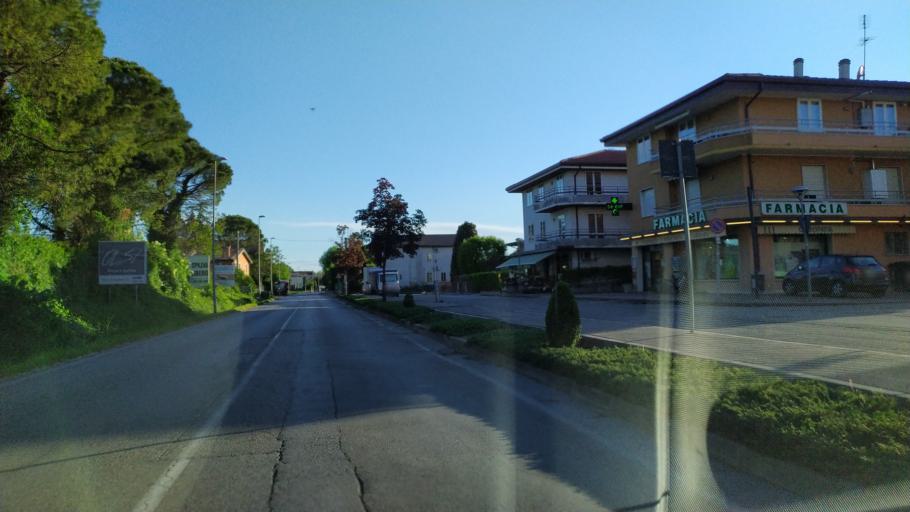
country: IT
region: Veneto
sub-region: Provincia di Padova
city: Tencarola
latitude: 45.3866
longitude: 11.8038
